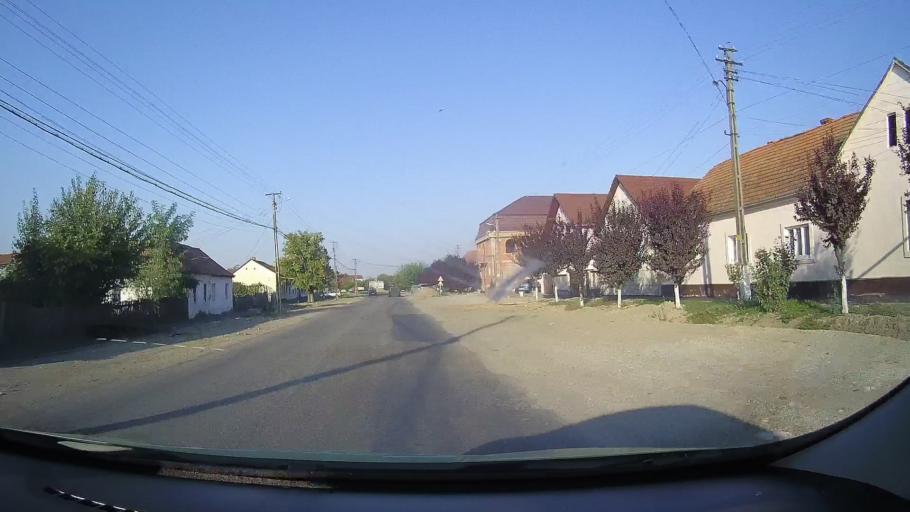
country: RO
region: Arad
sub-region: Comuna Siria
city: Siria
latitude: 46.2738
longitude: 21.6411
